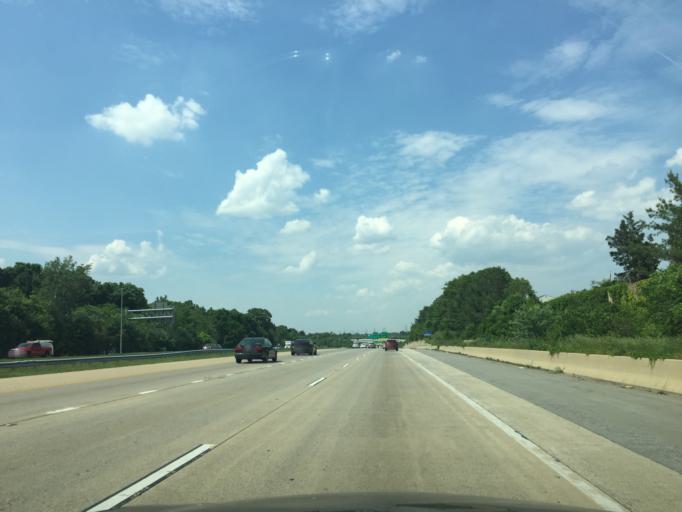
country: US
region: Maryland
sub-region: Anne Arundel County
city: Ferndale
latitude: 39.1931
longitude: -76.6324
